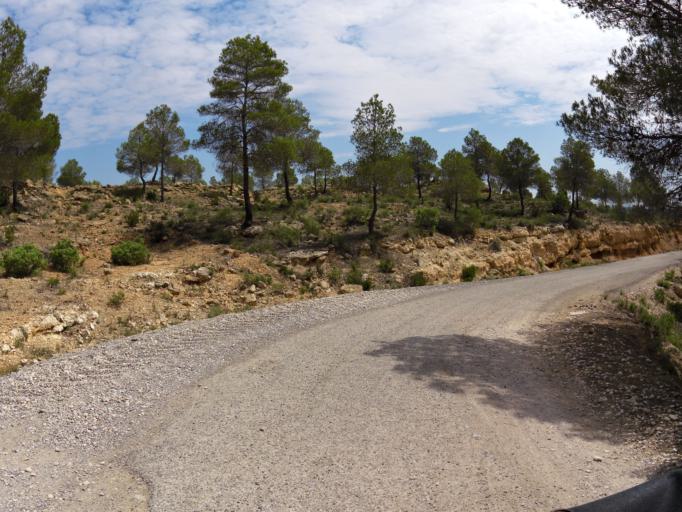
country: ES
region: Castille-La Mancha
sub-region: Provincia de Albacete
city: Casas Ibanez
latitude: 39.3628
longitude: -1.4674
